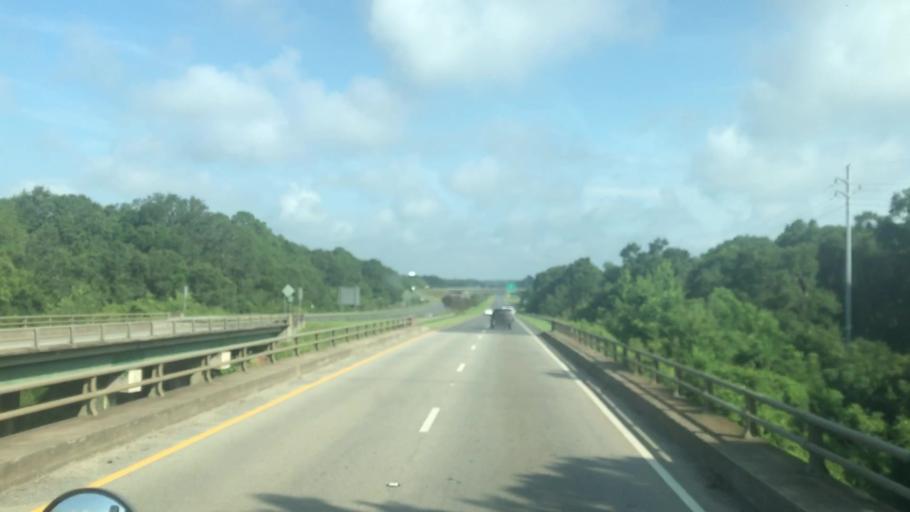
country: US
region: Georgia
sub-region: Decatur County
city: Bainbridge
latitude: 30.9069
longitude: -84.5892
